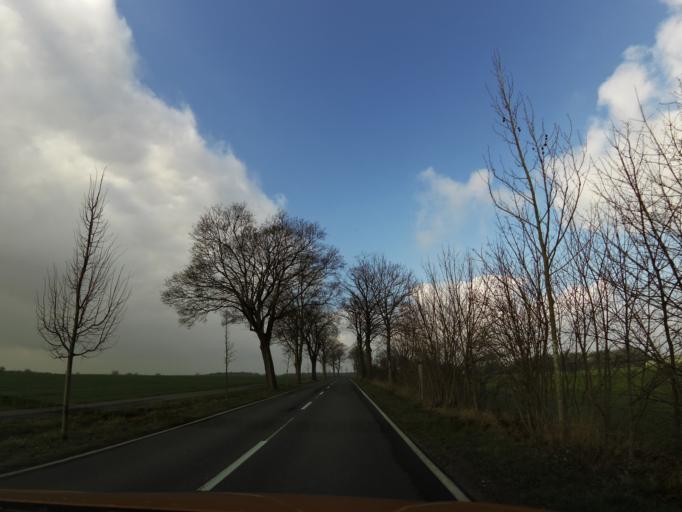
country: DE
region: Berlin
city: Wilhelmstadt
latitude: 52.5060
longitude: 13.1566
